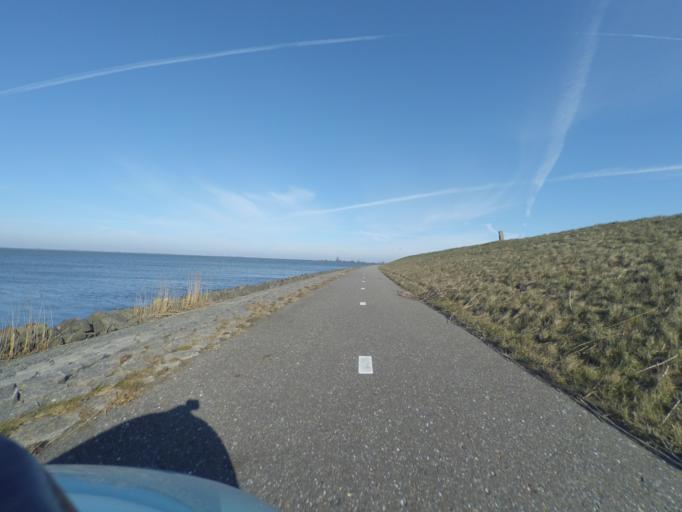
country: NL
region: North Holland
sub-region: Gemeente Waterland
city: Marken
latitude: 52.3771
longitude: 5.1223
